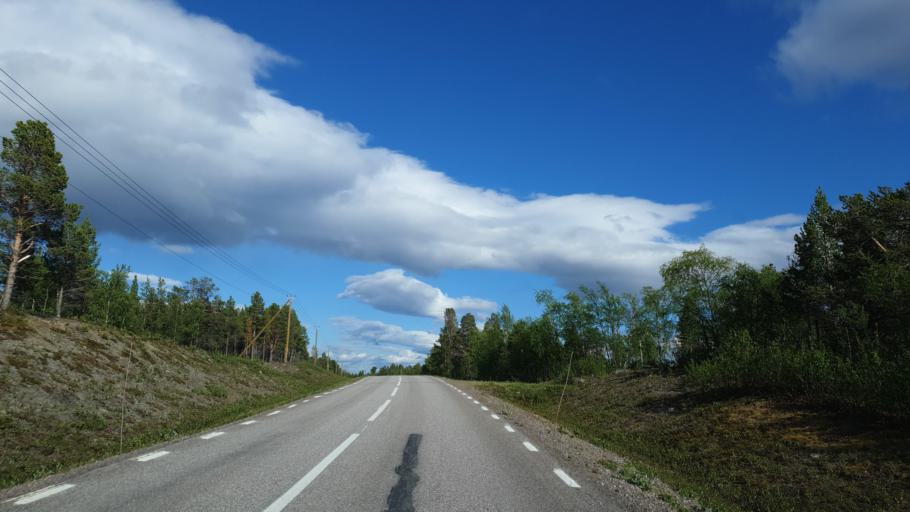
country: SE
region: Norrbotten
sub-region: Kiruna Kommun
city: Kiruna
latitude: 67.8700
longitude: 19.2545
